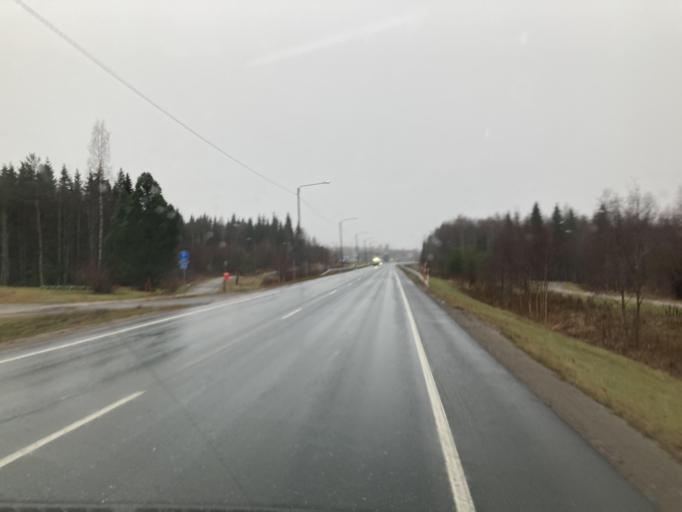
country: FI
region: Lapland
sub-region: Torniolaakso
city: Ylitornio
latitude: 66.3418
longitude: 23.6882
